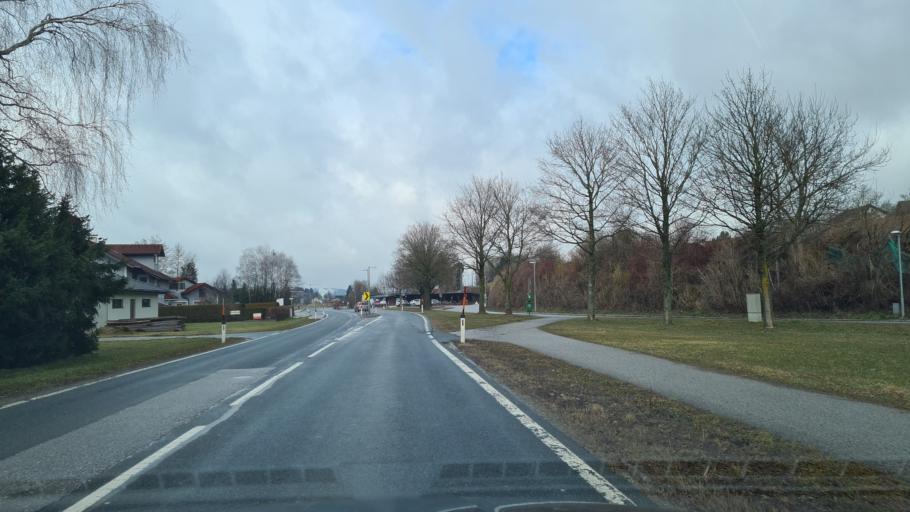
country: AT
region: Salzburg
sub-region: Politischer Bezirk Salzburg-Umgebung
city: Strasswalchen
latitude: 47.9700
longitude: 13.2756
